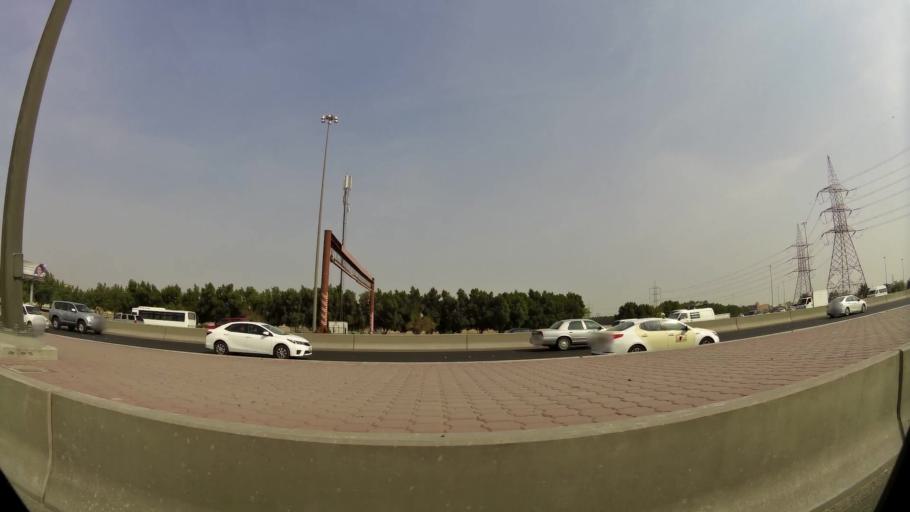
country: KW
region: Al Asimah
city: Ar Rabiyah
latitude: 29.3044
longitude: 47.9445
